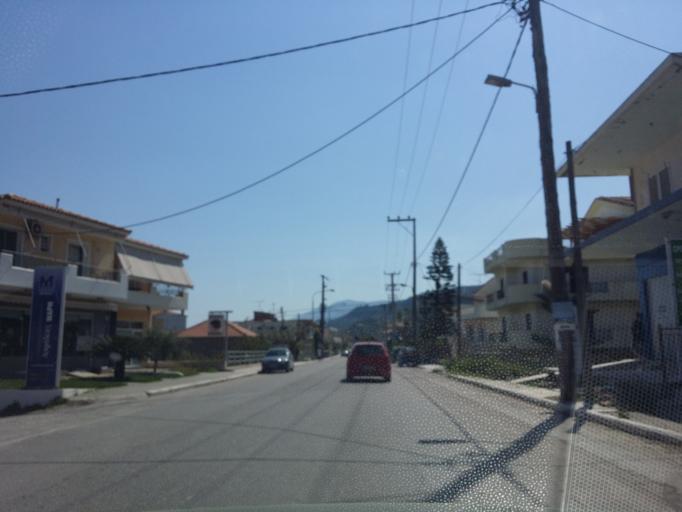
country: GR
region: West Greece
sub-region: Nomos Achaias
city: Aiyira
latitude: 38.1503
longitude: 22.3513
